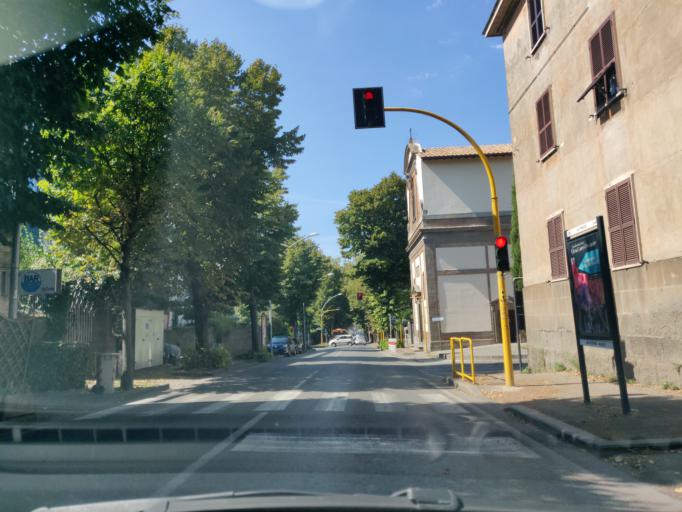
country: IT
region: Latium
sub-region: Provincia di Viterbo
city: Viterbo
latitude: 42.4244
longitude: 12.1109
